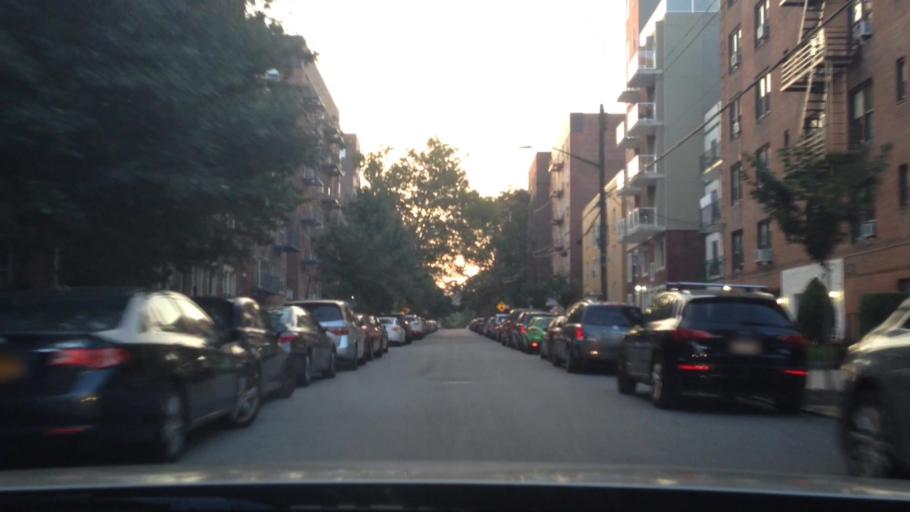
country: US
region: New York
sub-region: Queens County
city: Borough of Queens
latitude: 40.7278
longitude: -73.8609
